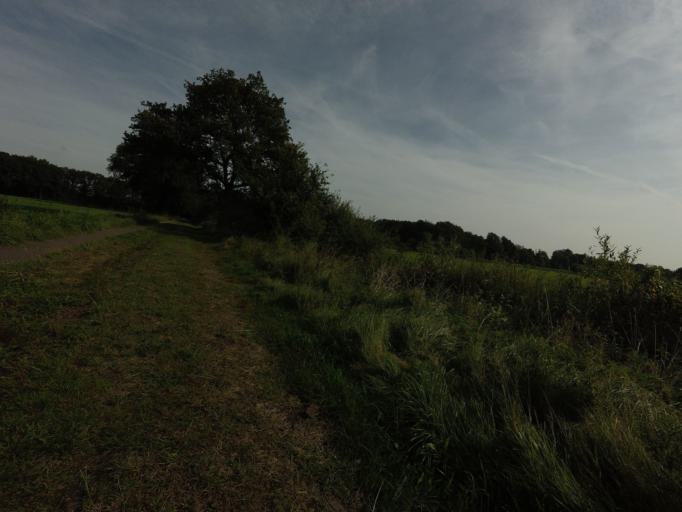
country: NL
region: Overijssel
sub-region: Gemeente Enschede
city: Enschede
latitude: 52.1843
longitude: 6.9404
